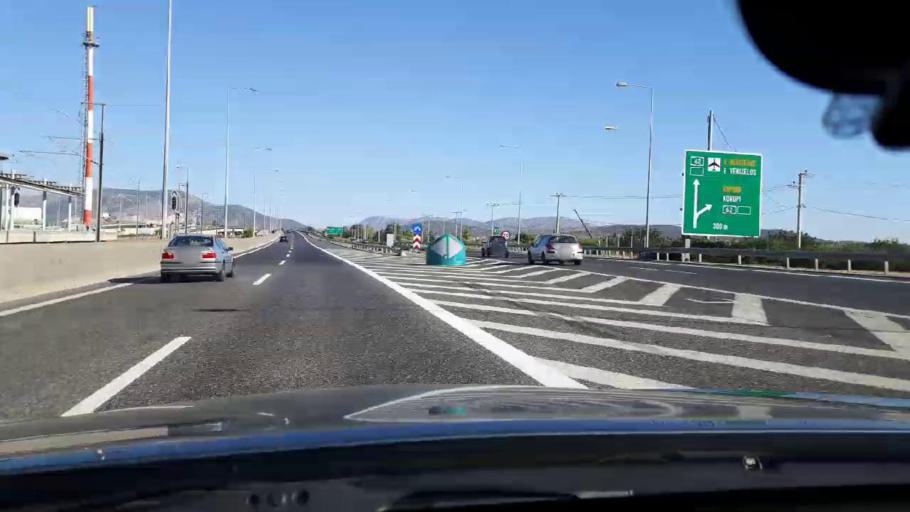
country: GR
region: Attica
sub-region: Nomarchia Anatolikis Attikis
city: Koropi
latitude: 37.9028
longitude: 23.9041
